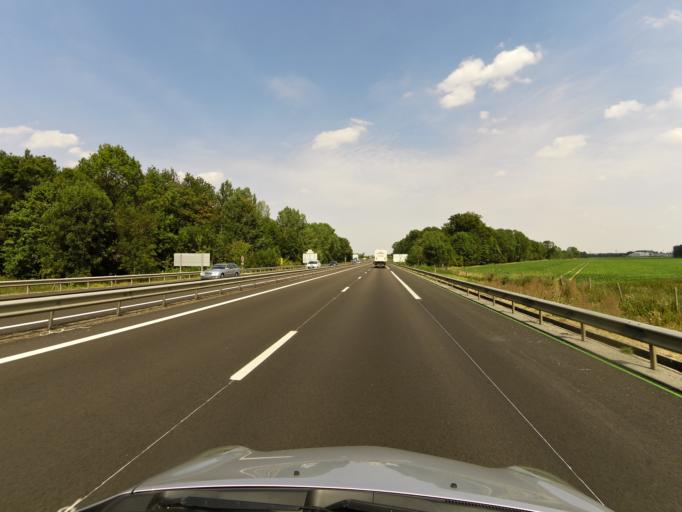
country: FR
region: Champagne-Ardenne
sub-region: Departement de la Marne
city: Saint-Brice-Courcelles
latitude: 49.2799
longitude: 3.9707
